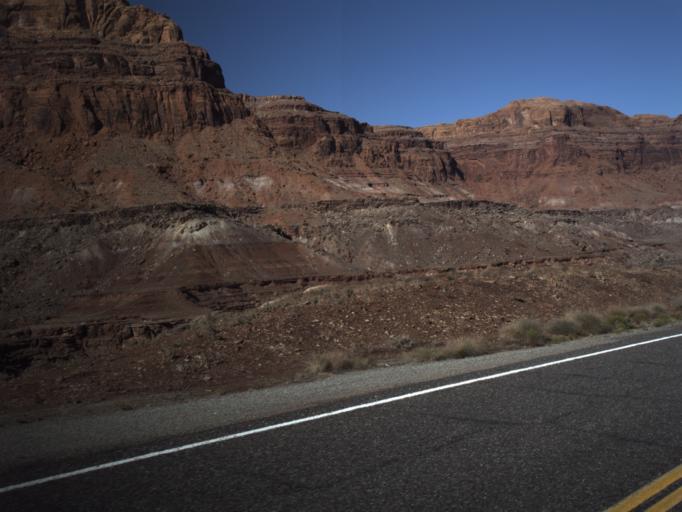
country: US
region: Utah
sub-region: San Juan County
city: Blanding
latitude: 37.8845
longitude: -110.4269
